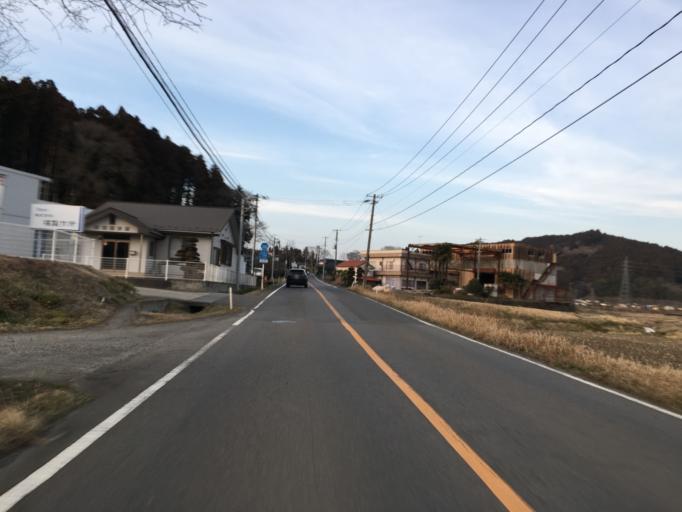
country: JP
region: Ibaraki
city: Daigo
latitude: 36.9472
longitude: 140.4077
